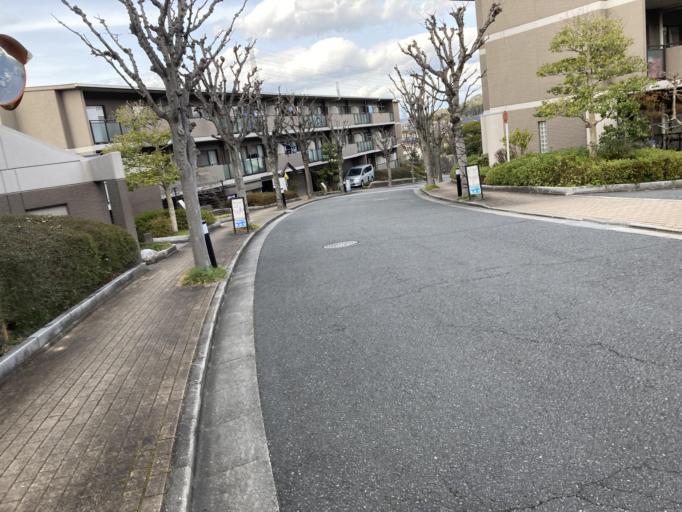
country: JP
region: Nara
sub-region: Ikoma-shi
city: Ikoma
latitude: 34.7078
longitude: 135.6993
